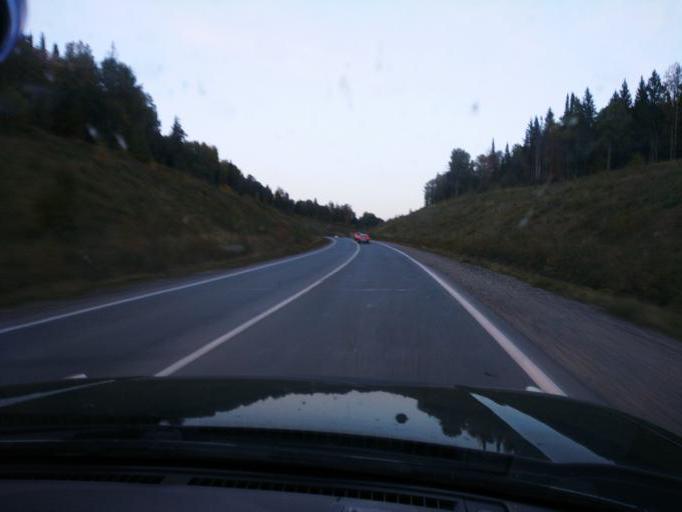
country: RU
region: Perm
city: Sylva
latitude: 58.2955
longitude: 56.8065
